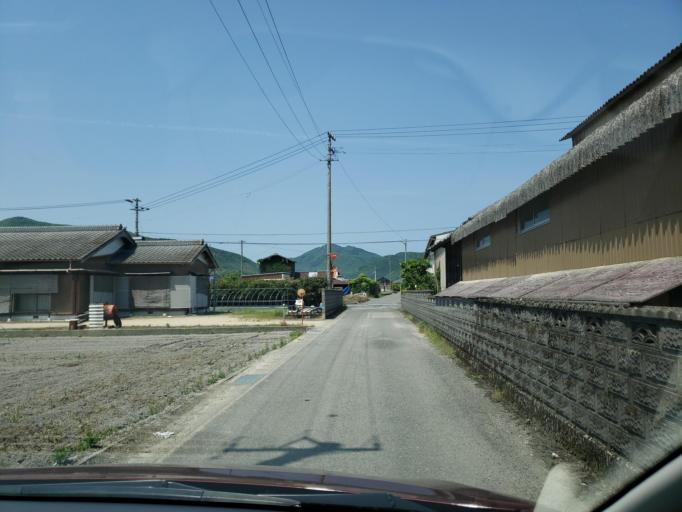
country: JP
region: Tokushima
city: Kamojimacho-jogejima
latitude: 34.0910
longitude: 134.2682
